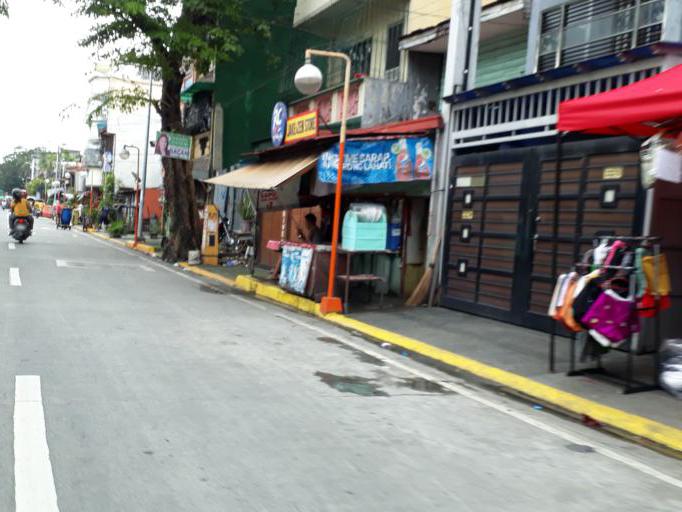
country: PH
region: Metro Manila
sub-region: City of Manila
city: Manila
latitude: 14.6082
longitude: 120.9985
